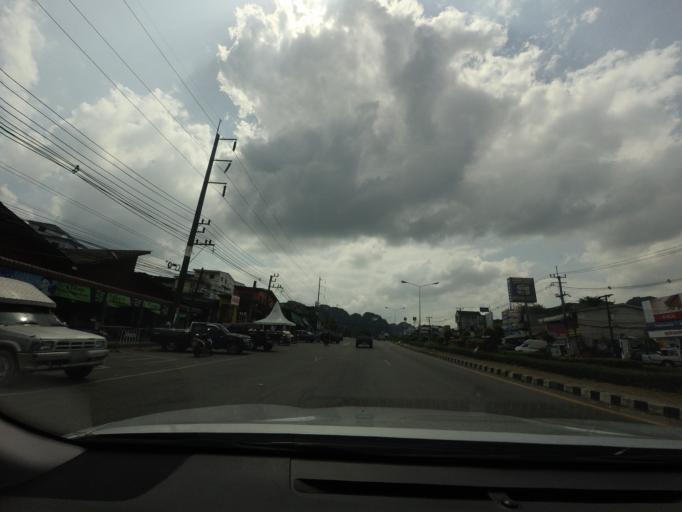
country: TH
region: Krabi
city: Ao Luek
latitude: 8.3978
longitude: 98.7428
